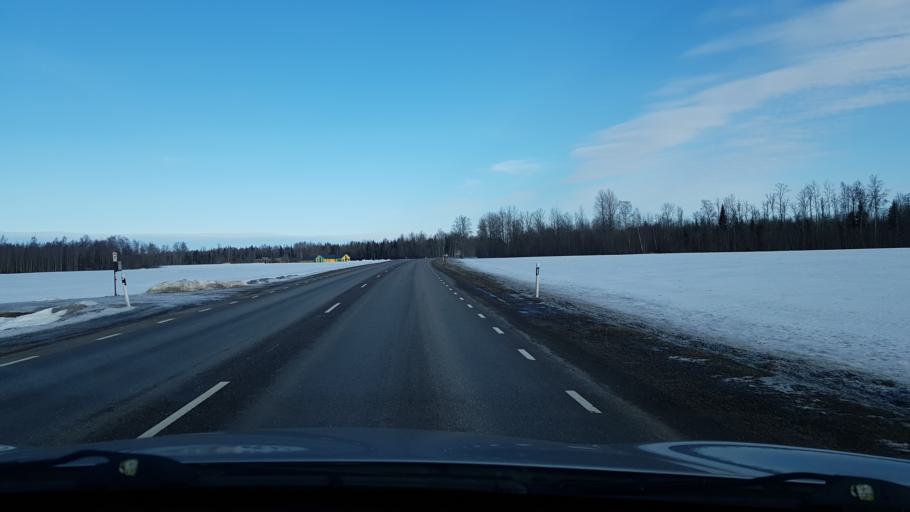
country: EE
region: Viljandimaa
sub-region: Viljandi linn
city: Viljandi
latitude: 58.4642
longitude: 25.5930
